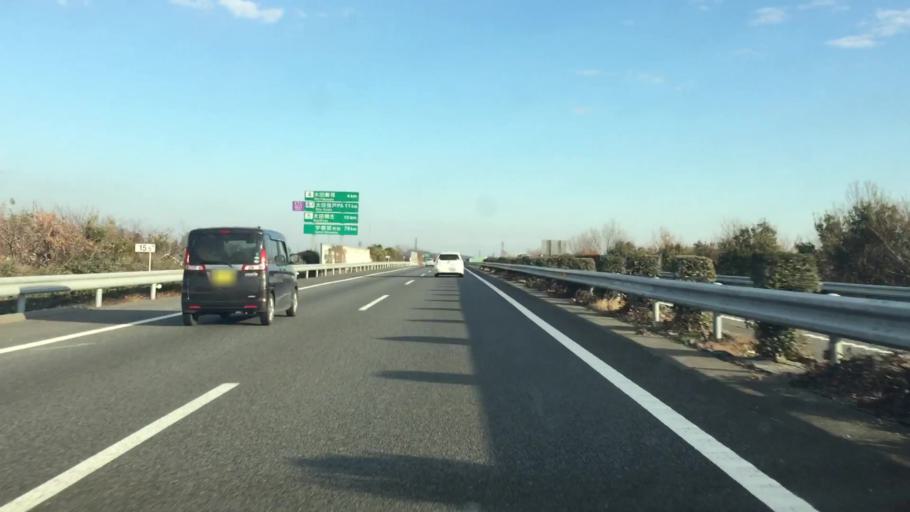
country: JP
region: Gunma
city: Isesaki
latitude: 36.3520
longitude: 139.2312
